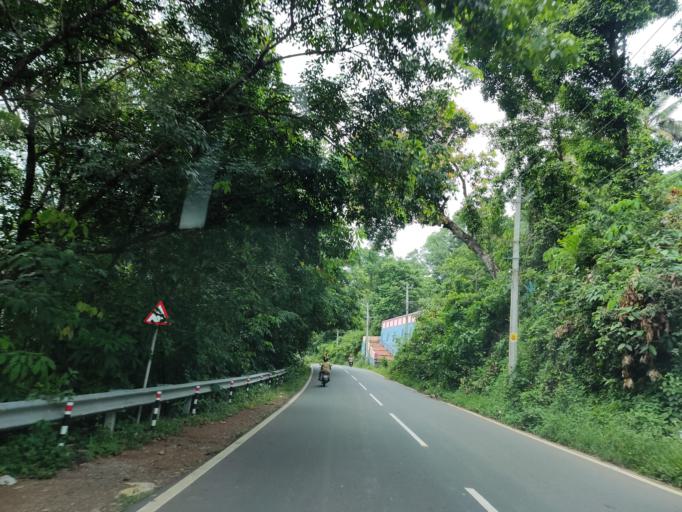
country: IN
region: Kerala
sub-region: Alappuzha
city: Chengannur
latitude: 9.2763
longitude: 76.6148
